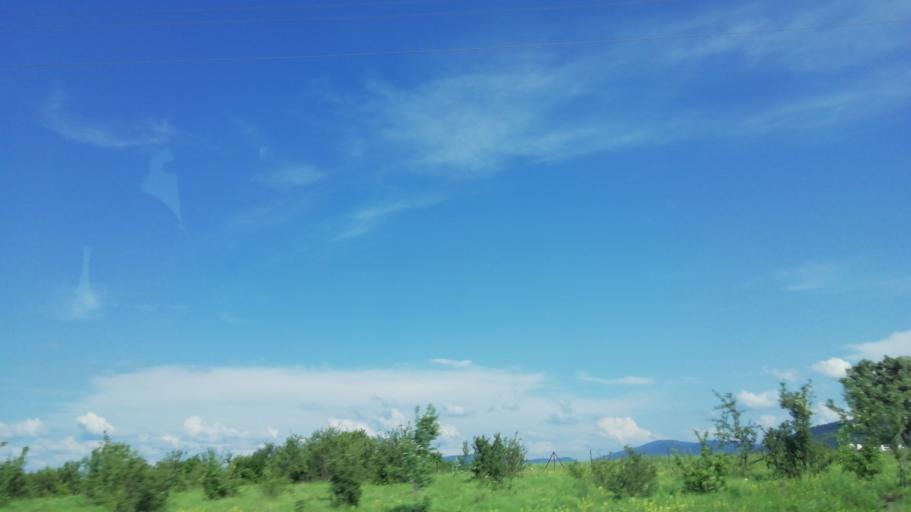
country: TR
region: Karabuk
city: Karabuk
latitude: 41.0996
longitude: 32.5944
